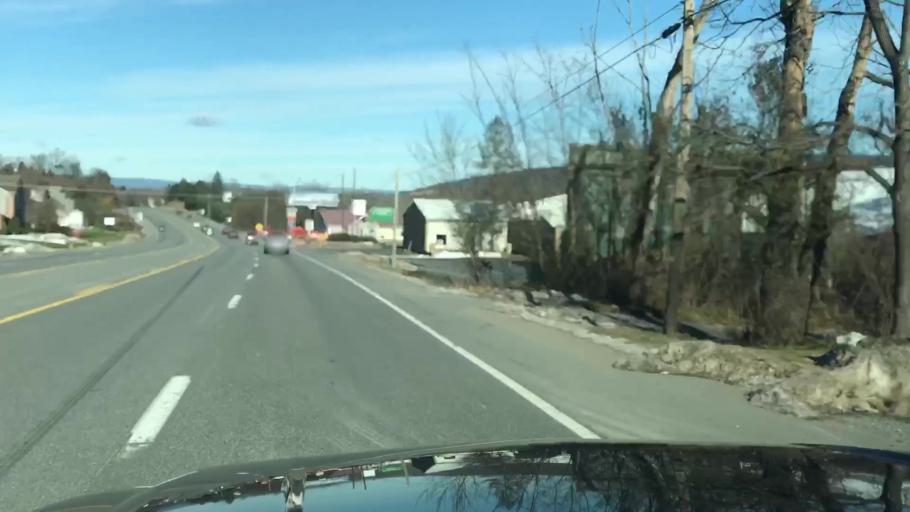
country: US
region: Pennsylvania
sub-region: Northumberland County
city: Northumberland
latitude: 40.9005
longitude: -76.8468
